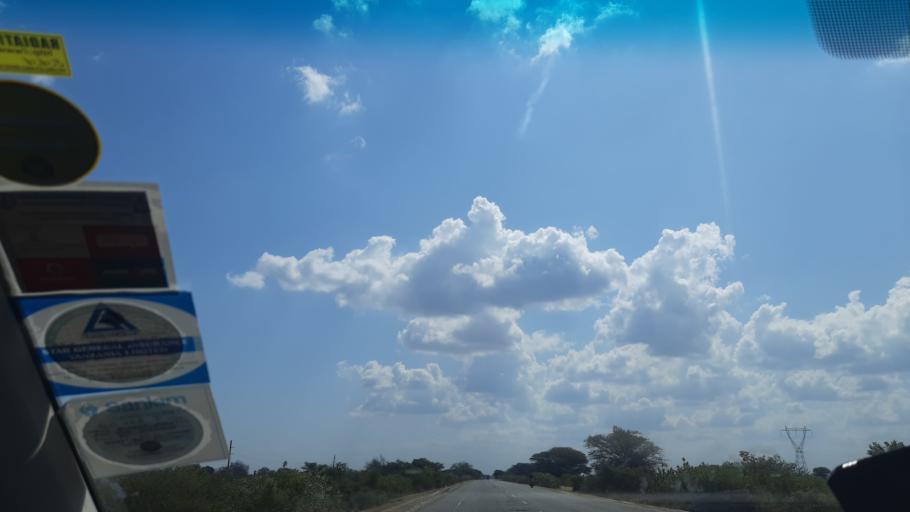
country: TZ
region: Singida
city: Kintinku
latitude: -5.9348
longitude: 35.2851
